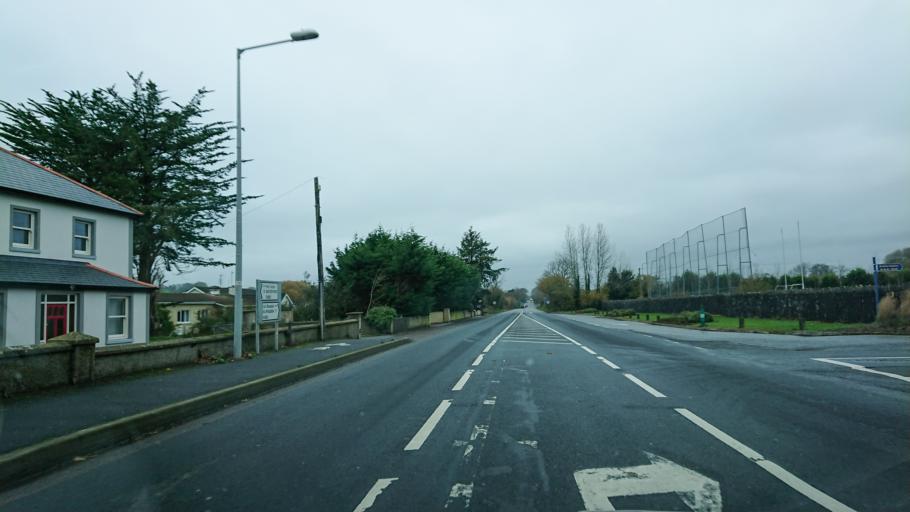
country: IE
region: Munster
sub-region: Waterford
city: Waterford
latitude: 52.2382
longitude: -7.1786
